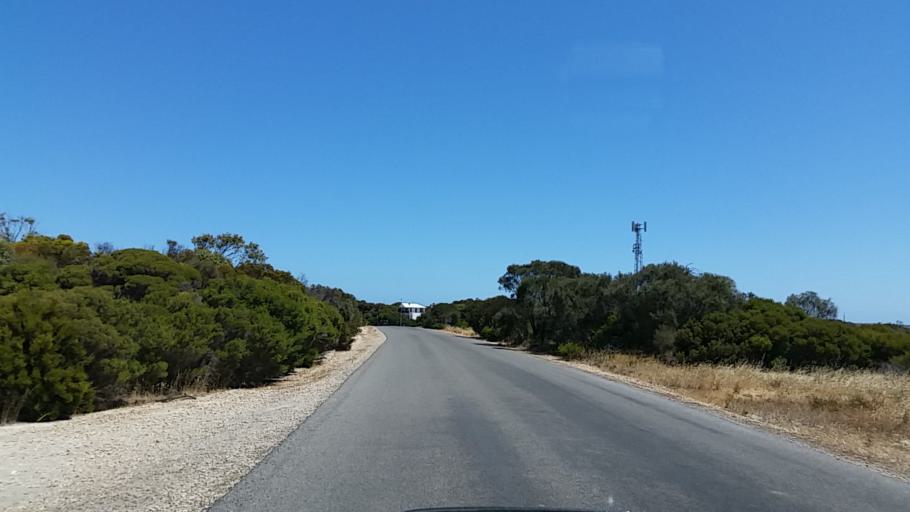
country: AU
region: South Australia
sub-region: Yorke Peninsula
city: Honiton
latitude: -35.2430
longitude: 136.9765
